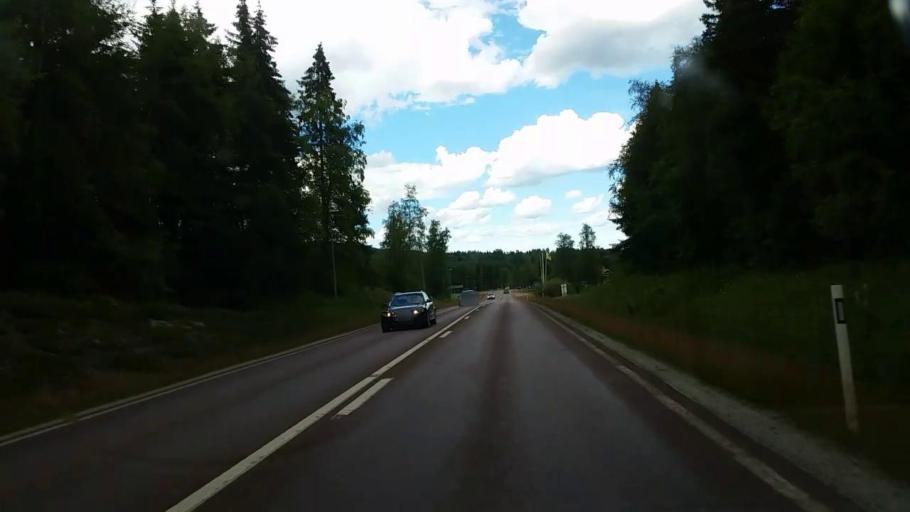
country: SE
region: Gaevleborg
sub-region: Ljusdals Kommun
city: Jaervsoe
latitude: 61.6856
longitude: 16.1474
